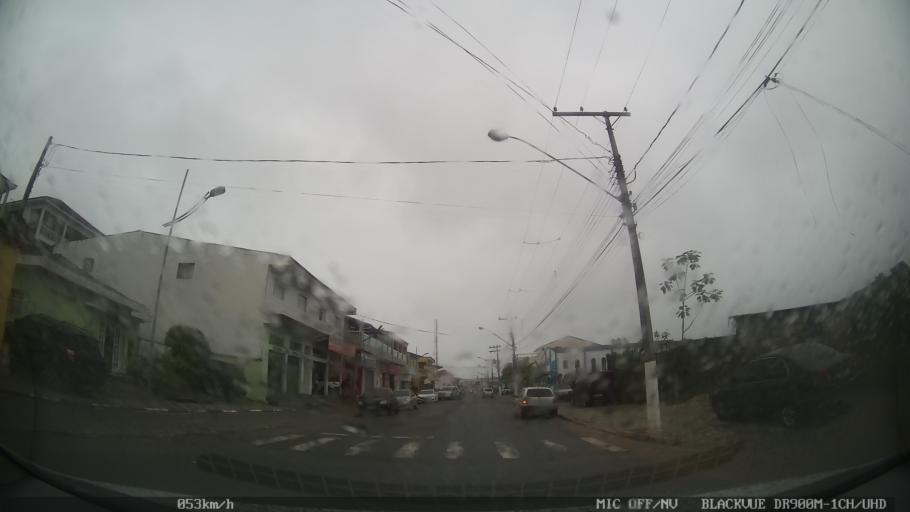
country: BR
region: Sao Paulo
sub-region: Juquia
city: Juquia
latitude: -24.3168
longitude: -47.6332
